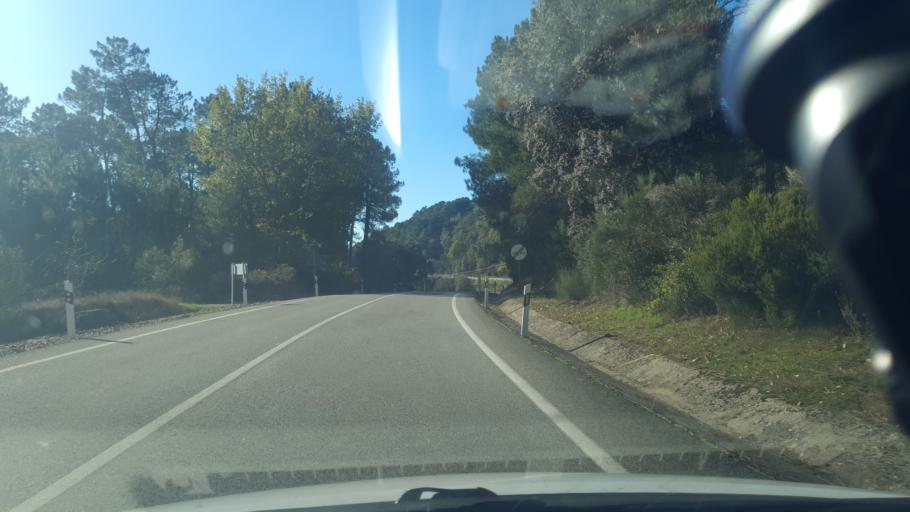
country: ES
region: Castille and Leon
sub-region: Provincia de Avila
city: Arenas de San Pedro
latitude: 40.2084
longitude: -5.0408
